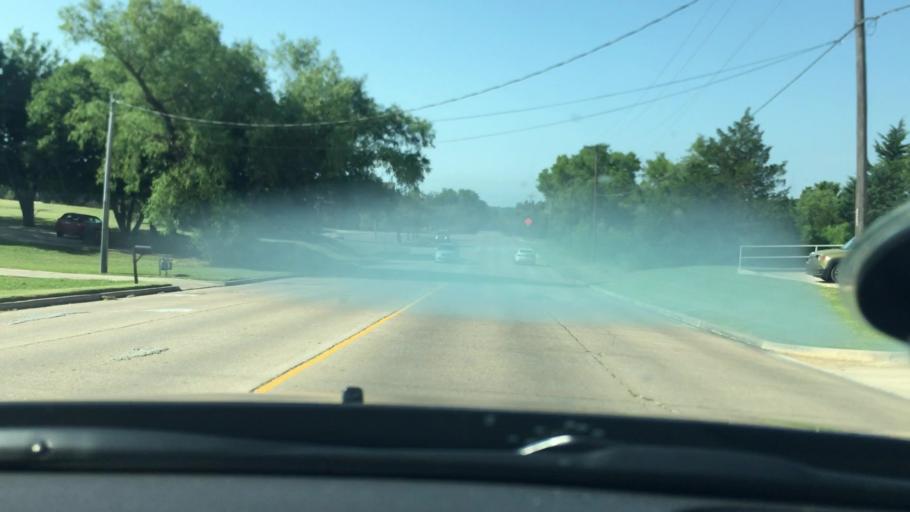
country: US
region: Oklahoma
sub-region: Pontotoc County
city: Ada
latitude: 34.7668
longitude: -96.6612
